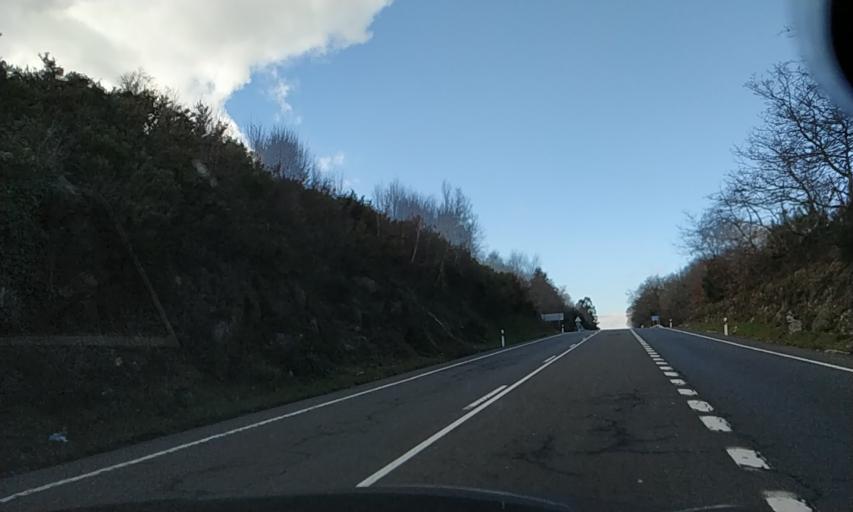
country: ES
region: Galicia
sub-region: Provincia de Pontevedra
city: Silleda
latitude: 42.7025
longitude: -8.3415
